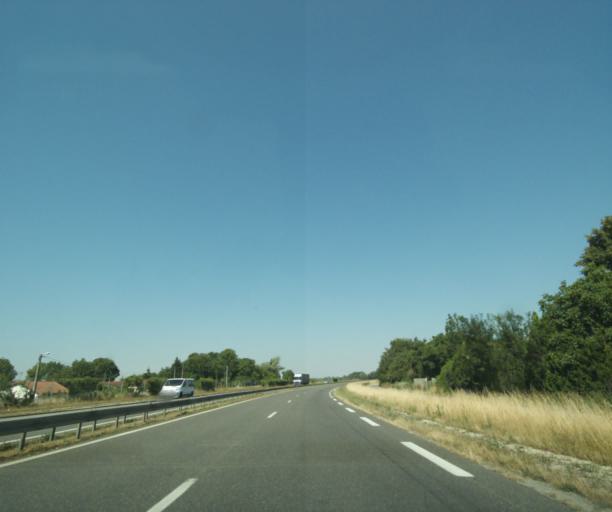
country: FR
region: Champagne-Ardenne
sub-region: Departement de la Haute-Marne
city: Villiers-en-Lieu
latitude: 48.6537
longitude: 4.8232
